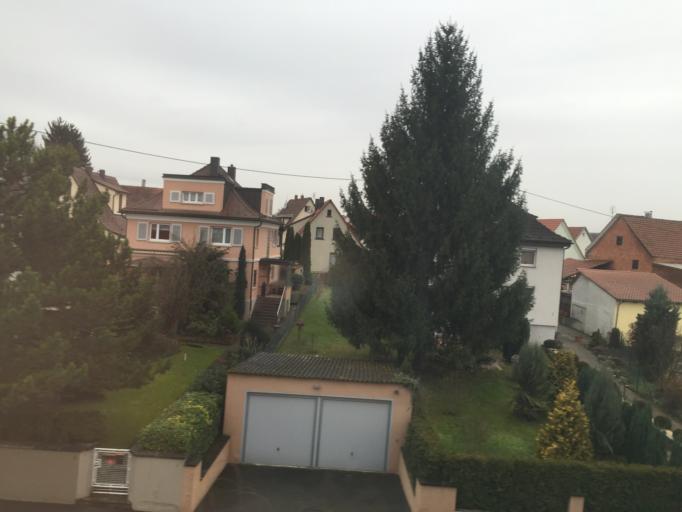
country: DE
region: Baden-Wuerttemberg
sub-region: Regierungsbezirk Stuttgart
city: Kirchheim am Neckar
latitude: 49.0402
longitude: 9.1504
